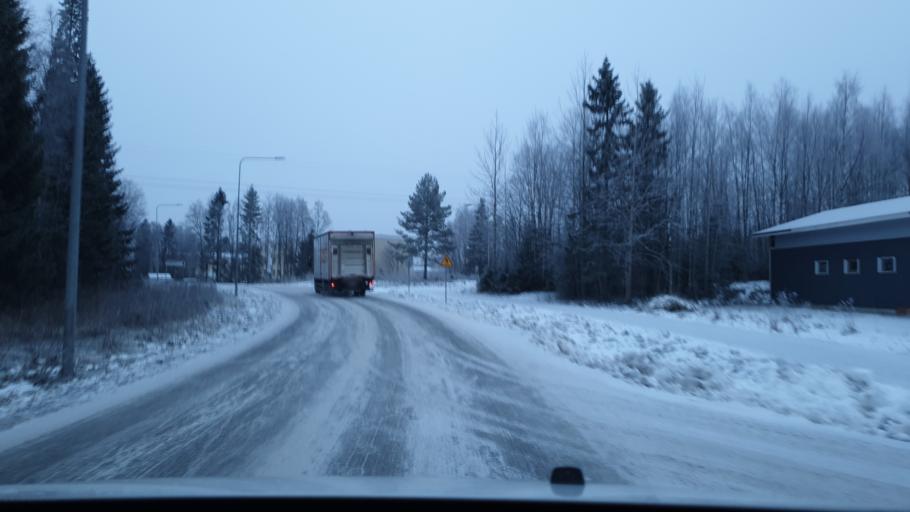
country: FI
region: Lapland
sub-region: Kemi-Tornio
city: Kemi
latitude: 65.7357
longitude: 24.6084
